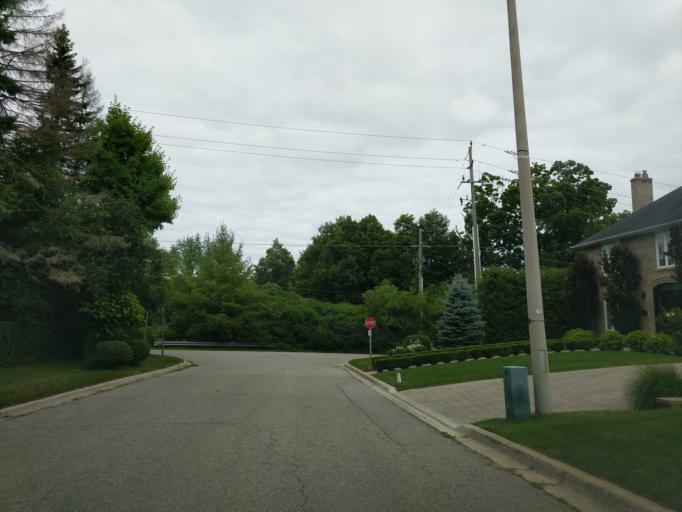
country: CA
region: Ontario
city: Willowdale
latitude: 43.8129
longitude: -79.3747
